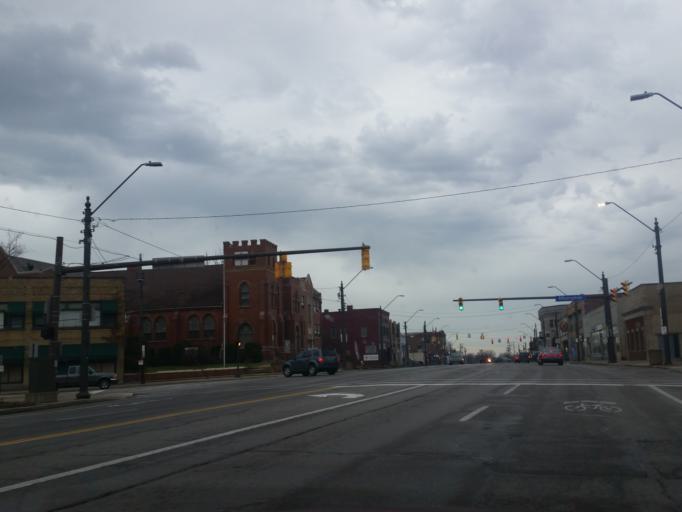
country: US
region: Ohio
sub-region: Cuyahoga County
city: Brooklyn Heights
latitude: 41.4403
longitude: -81.7059
